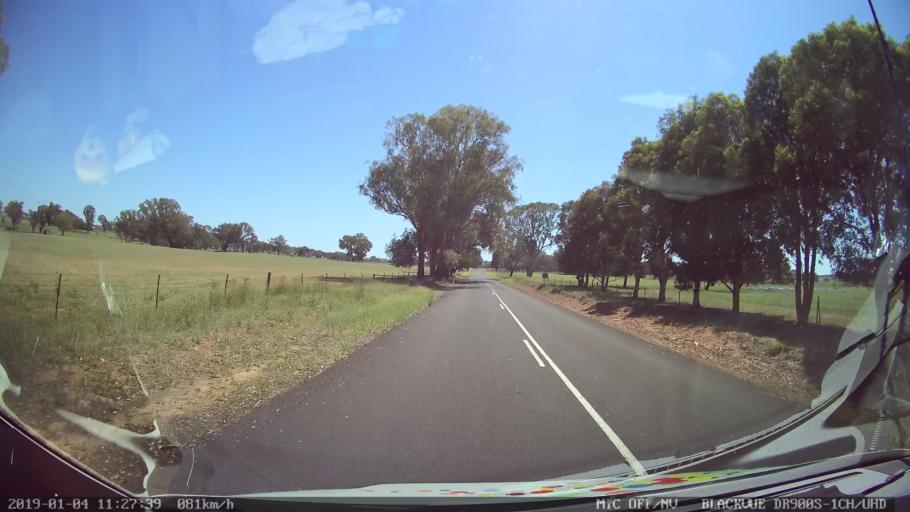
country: AU
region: New South Wales
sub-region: Cabonne
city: Molong
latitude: -33.1075
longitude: 148.7649
